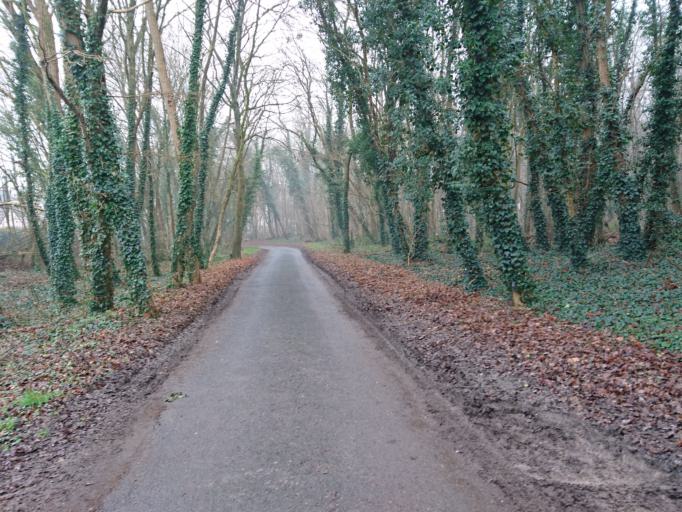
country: FR
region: Ile-de-France
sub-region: Departement de Seine-et-Marne
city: Veneux-les-Sablons
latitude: 48.3728
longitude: 2.8017
